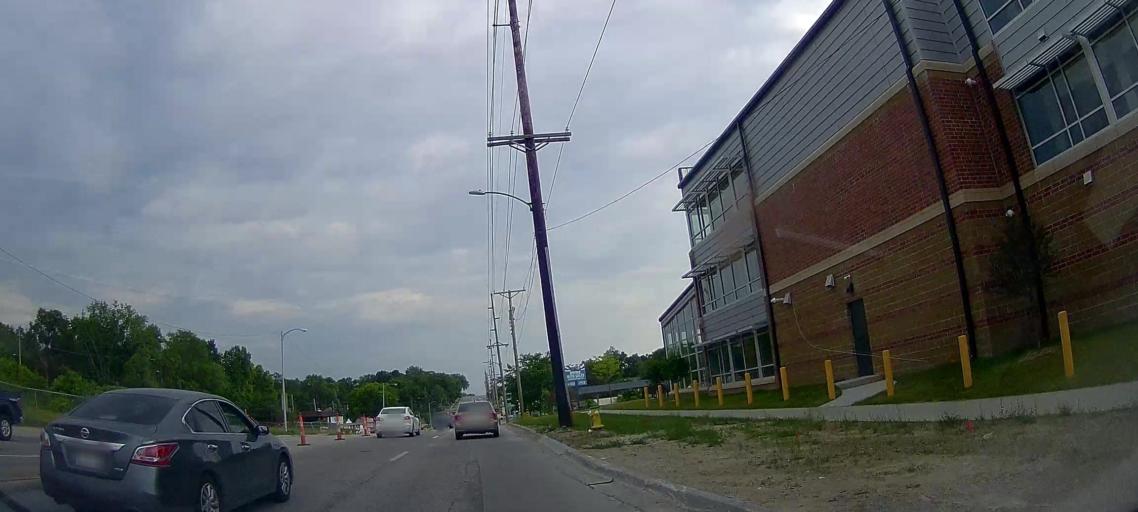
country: US
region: Nebraska
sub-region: Douglas County
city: Ralston
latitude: 41.2847
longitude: -96.0240
